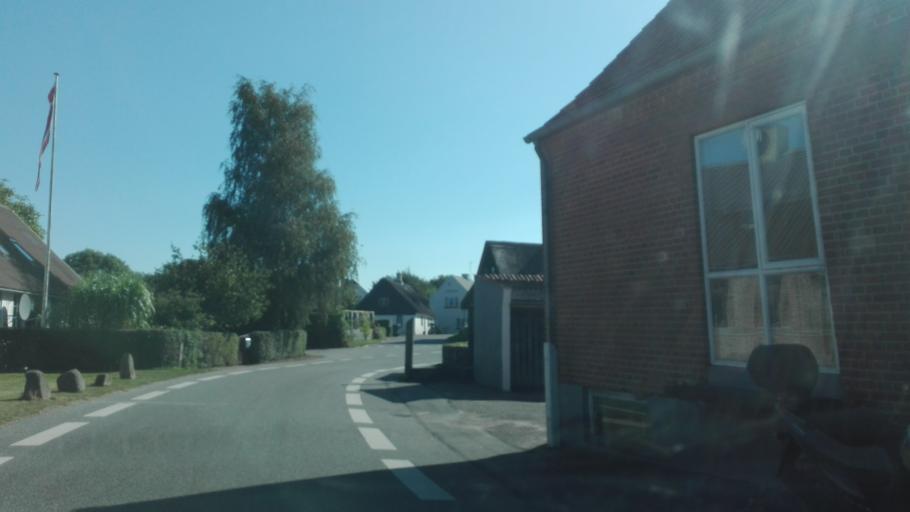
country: DK
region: Central Jutland
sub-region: Syddjurs Kommune
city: Ebeltoft
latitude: 56.2235
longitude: 10.7024
